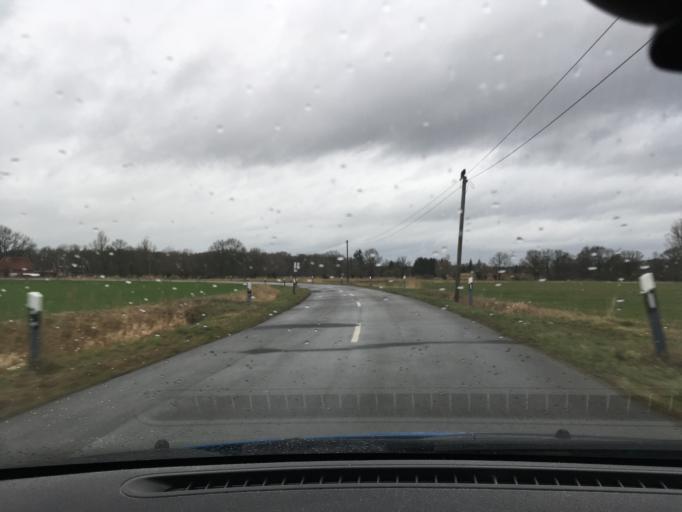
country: DE
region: Mecklenburg-Vorpommern
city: Nostorf
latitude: 53.3591
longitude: 10.6499
